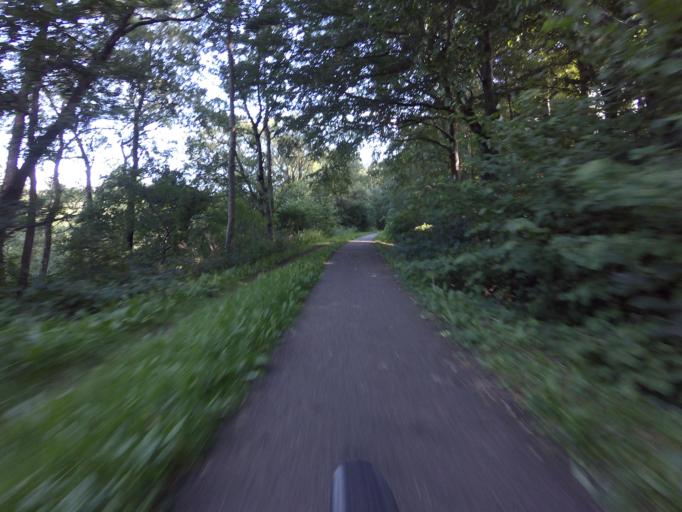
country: DK
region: Central Jutland
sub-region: Horsens Kommune
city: Horsens
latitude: 55.9370
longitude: 9.7749
